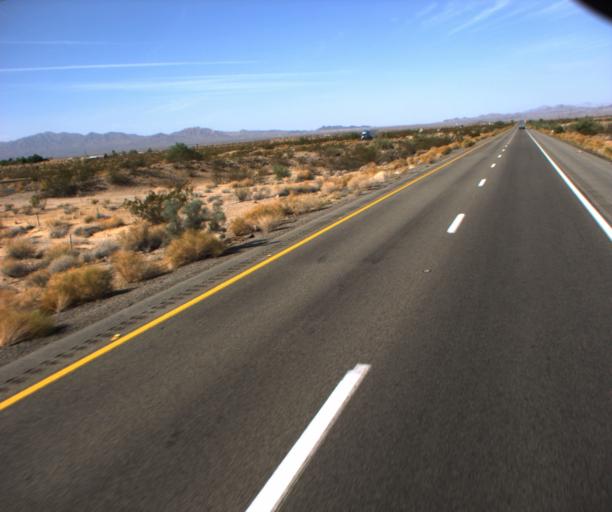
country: US
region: Arizona
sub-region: Mohave County
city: Desert Hills
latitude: 34.7620
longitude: -114.2070
